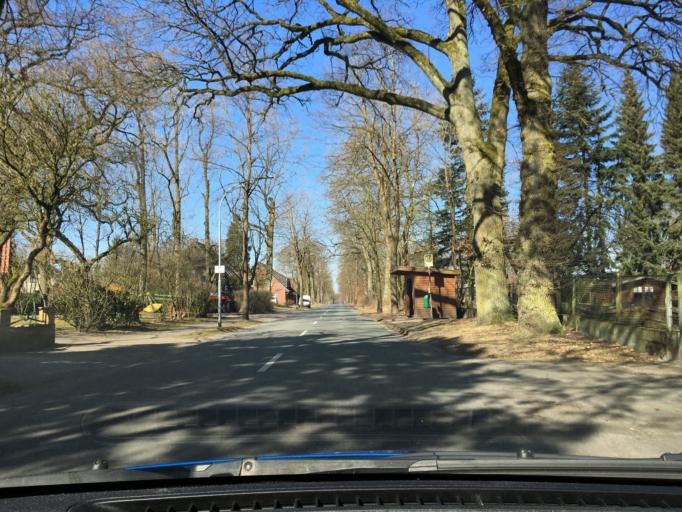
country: DE
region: Lower Saxony
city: Schneverdingen
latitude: 53.0840
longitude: 9.7658
